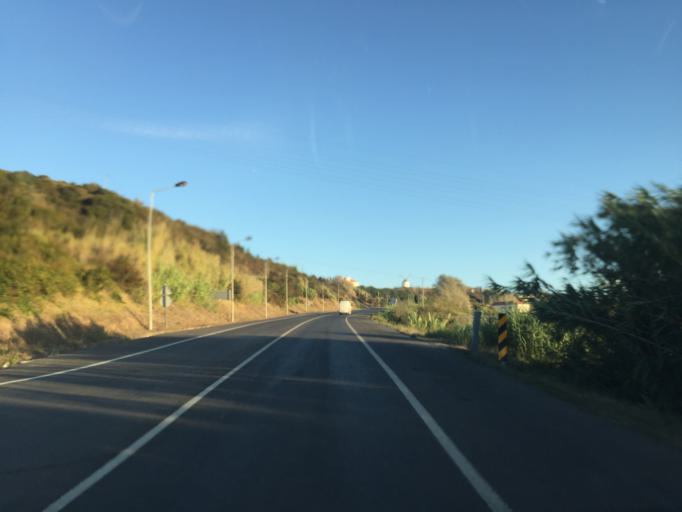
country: PT
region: Lisbon
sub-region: Torres Vedras
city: Torres Vedras
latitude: 39.0687
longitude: -9.2416
